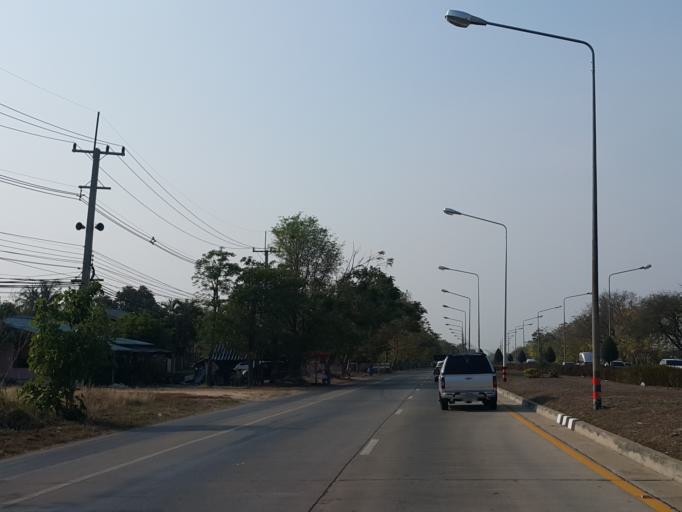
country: TH
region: Suphan Buri
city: Sam Chuk
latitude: 14.7645
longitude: 100.0935
